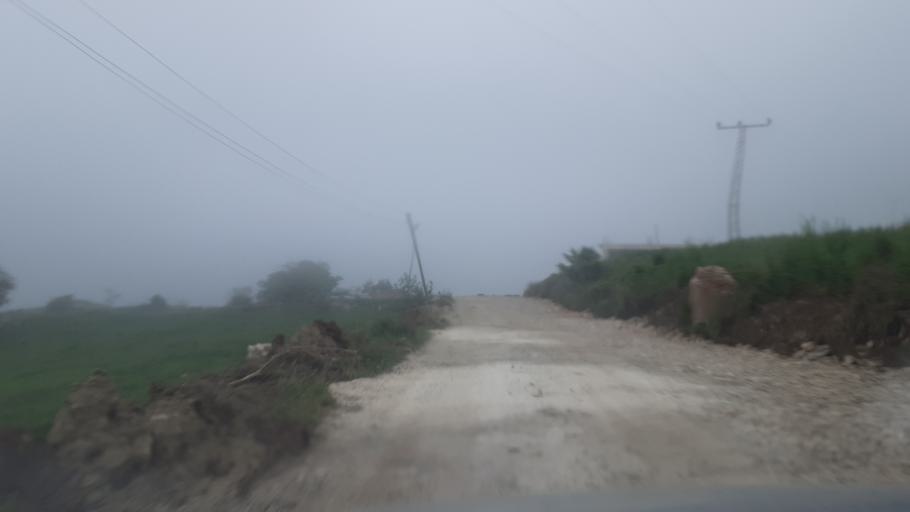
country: TR
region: Hatay
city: Yeditepe
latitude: 35.9716
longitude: 36.0021
